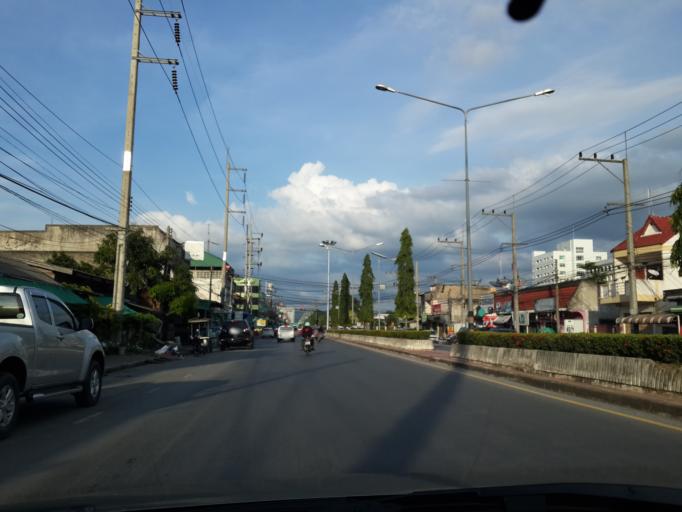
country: TH
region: Yala
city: Yala
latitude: 6.5470
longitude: 101.2745
